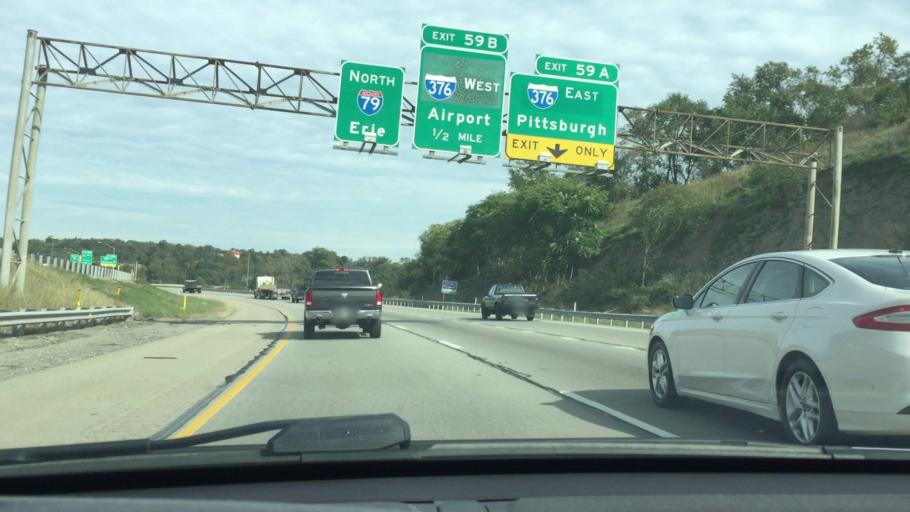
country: US
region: Pennsylvania
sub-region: Allegheny County
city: Carnegie
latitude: 40.4164
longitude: -80.1032
